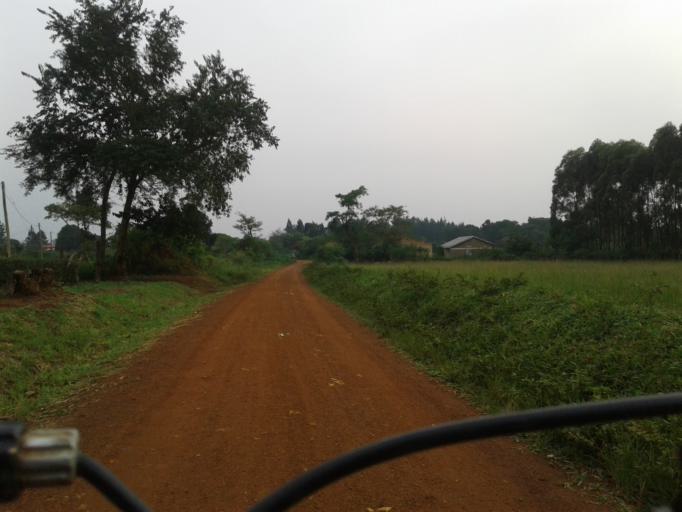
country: UG
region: Western Region
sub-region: Hoima District
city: Hoima
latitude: 1.4225
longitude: 31.3231
